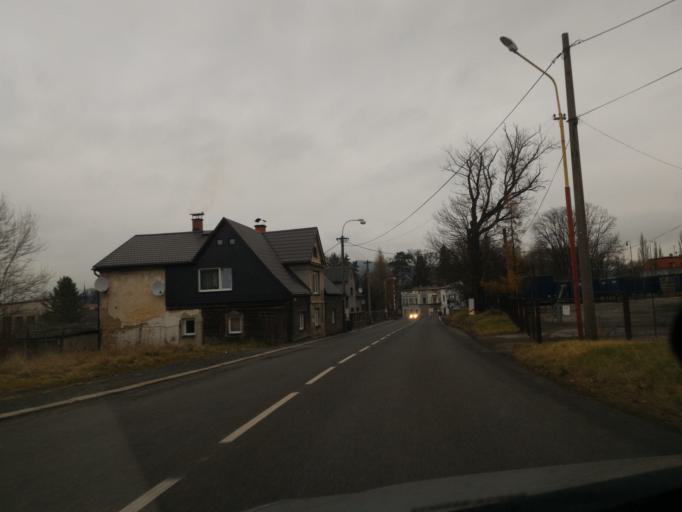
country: CZ
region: Ustecky
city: Varnsdorf
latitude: 50.9027
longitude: 14.6305
